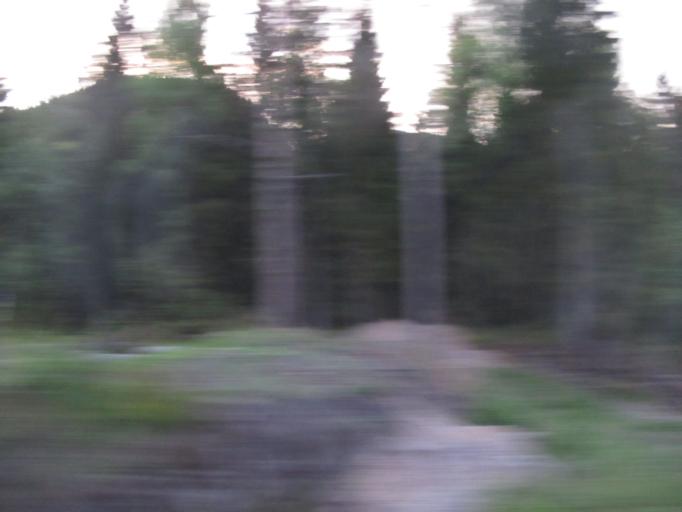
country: NO
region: Oppland
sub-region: Oyer
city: Tretten
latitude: 61.2808
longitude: 10.2896
